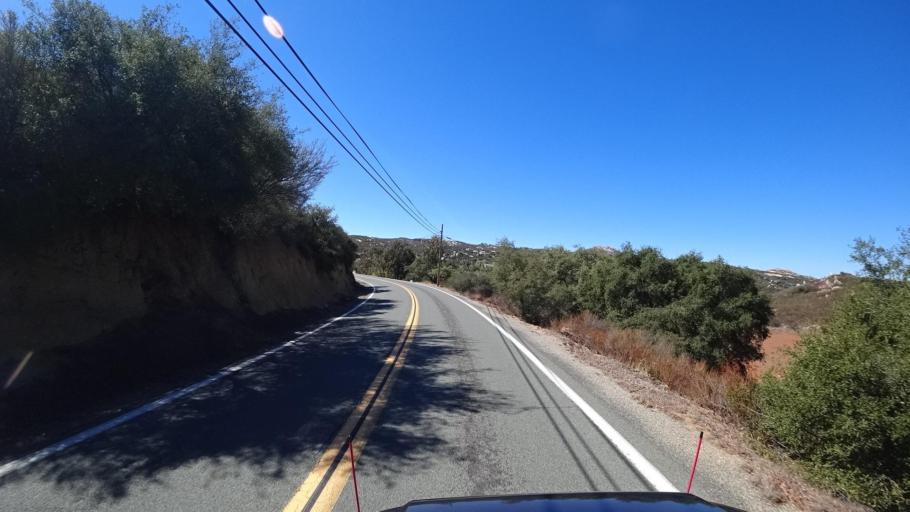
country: US
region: California
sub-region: San Diego County
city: Descanso
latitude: 32.7583
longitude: -116.6752
